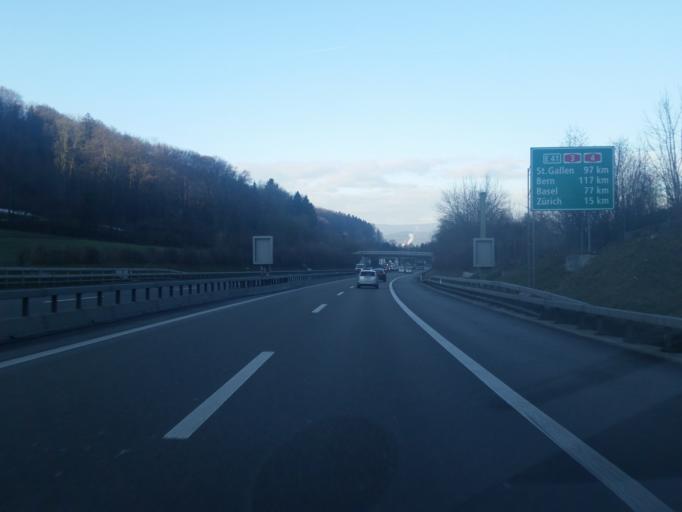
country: CH
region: Zurich
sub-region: Bezirk Dietikon
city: Urdorf / Oberurdorf
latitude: 47.3792
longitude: 8.4173
